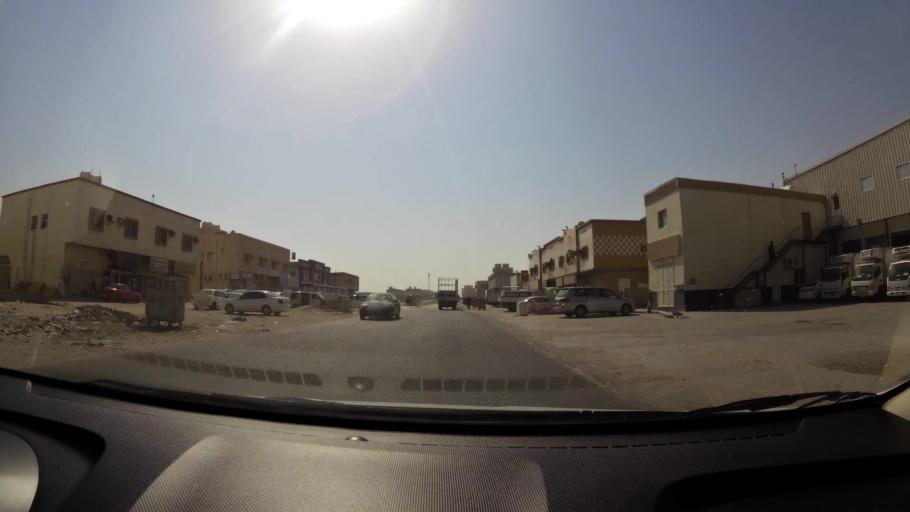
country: AE
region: Ajman
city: Ajman
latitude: 25.4322
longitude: 55.5463
